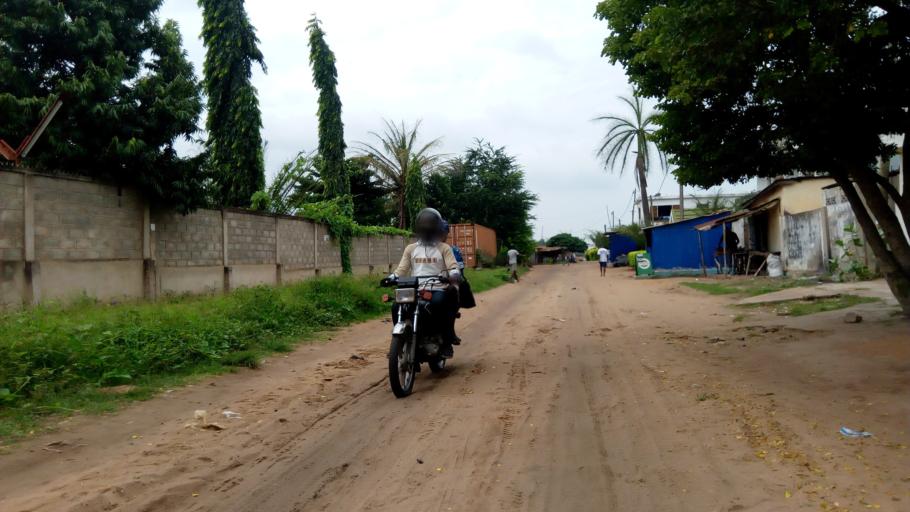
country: TG
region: Maritime
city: Lome
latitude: 6.1652
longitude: 1.2082
